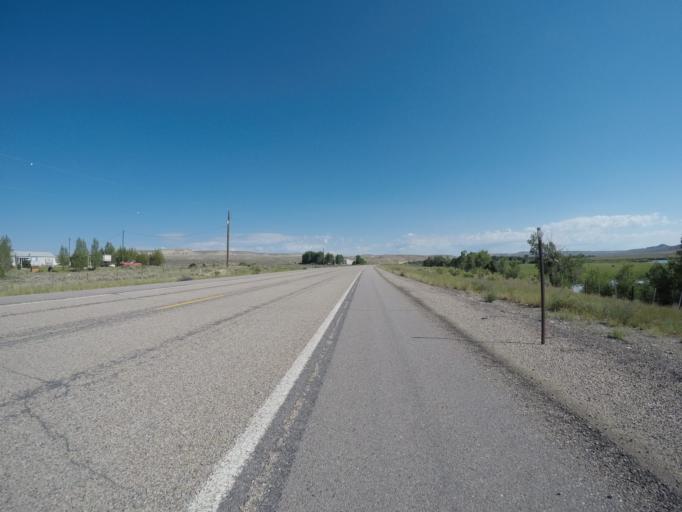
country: US
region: Wyoming
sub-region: Sublette County
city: Marbleton
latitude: 42.1600
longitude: -110.1882
